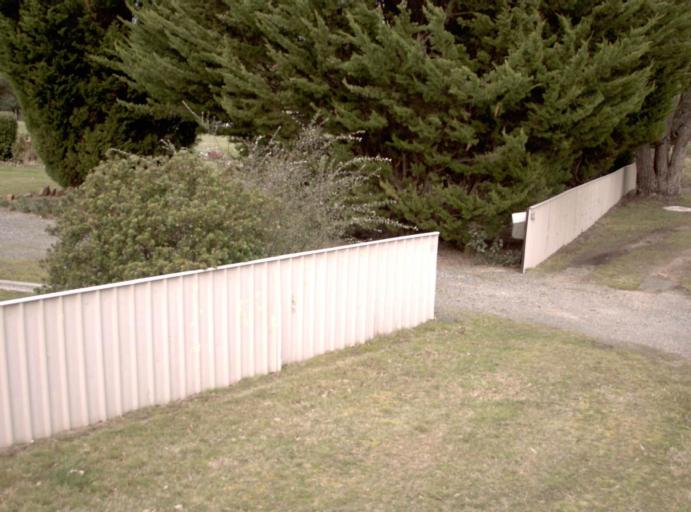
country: AU
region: Tasmania
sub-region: Launceston
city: Mayfield
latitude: -41.2662
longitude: 147.1605
